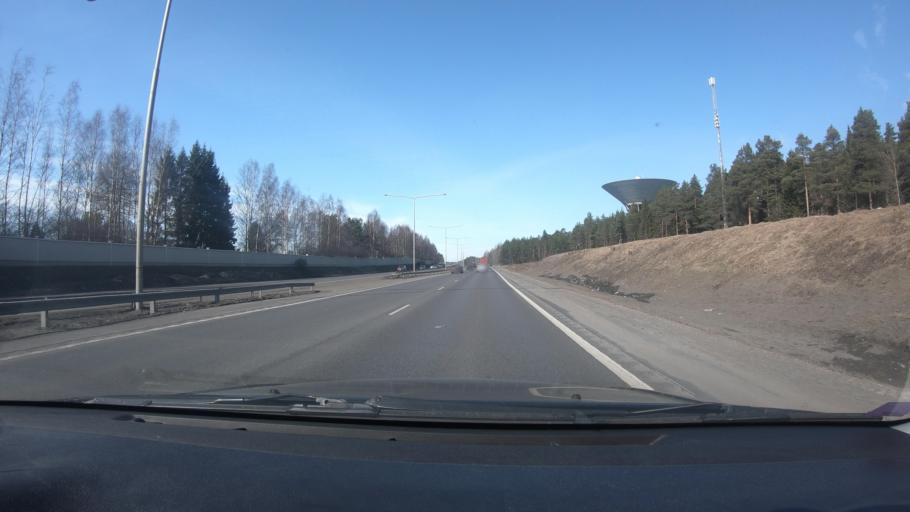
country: FI
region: Northern Ostrobothnia
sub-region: Oulu
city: Oulu
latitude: 65.0347
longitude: 25.4888
